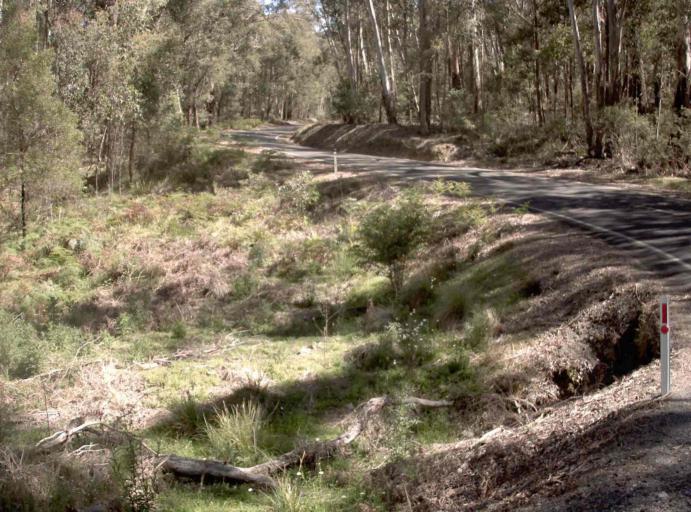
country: AU
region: New South Wales
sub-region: Bombala
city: Bombala
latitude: -37.1244
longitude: 148.7507
